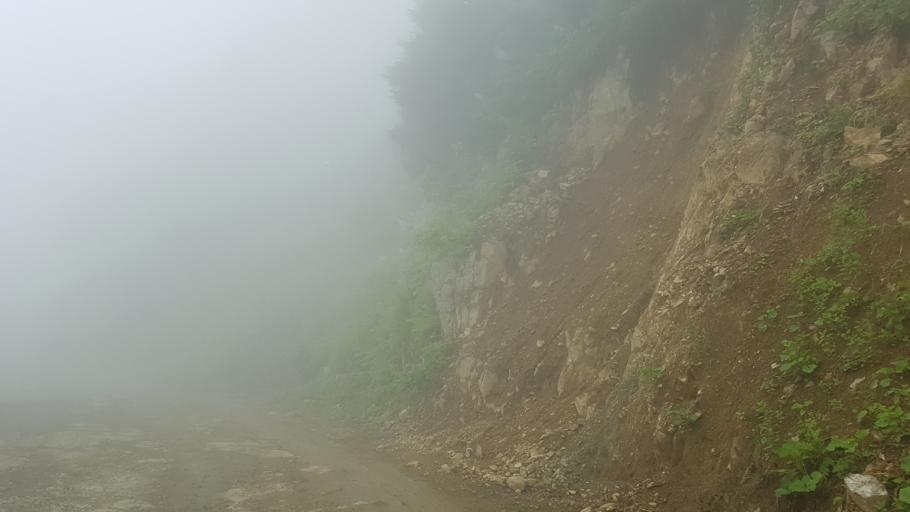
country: GE
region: Guria
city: Ozurgeti
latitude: 41.8299
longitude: 42.1479
